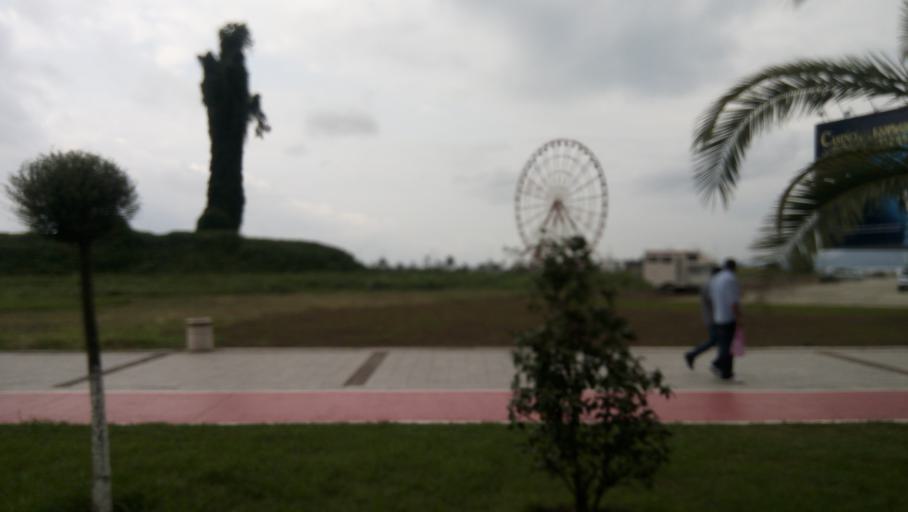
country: GE
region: Ajaria
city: Batumi
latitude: 41.6529
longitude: 41.6408
